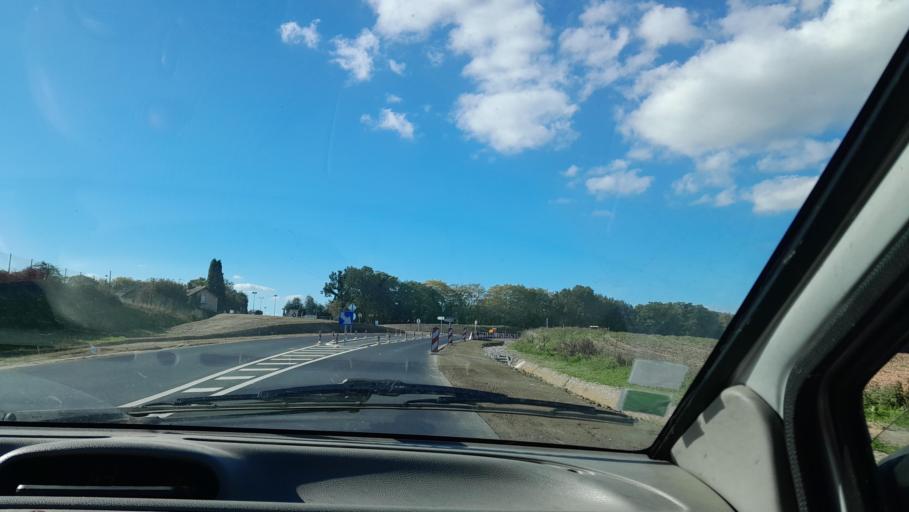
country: FR
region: Pays de la Loire
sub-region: Departement de la Mayenne
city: Cosse-le-Vivien
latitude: 47.9454
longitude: -0.9011
